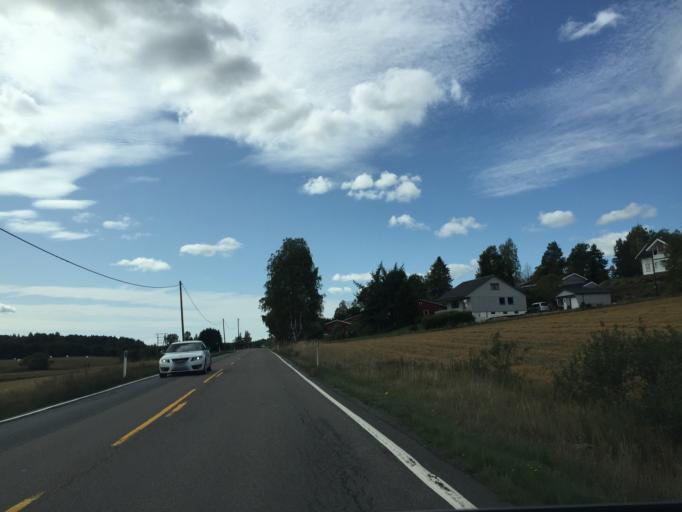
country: NO
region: Ostfold
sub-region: Hobol
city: Elvestad
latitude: 59.6123
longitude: 10.9298
